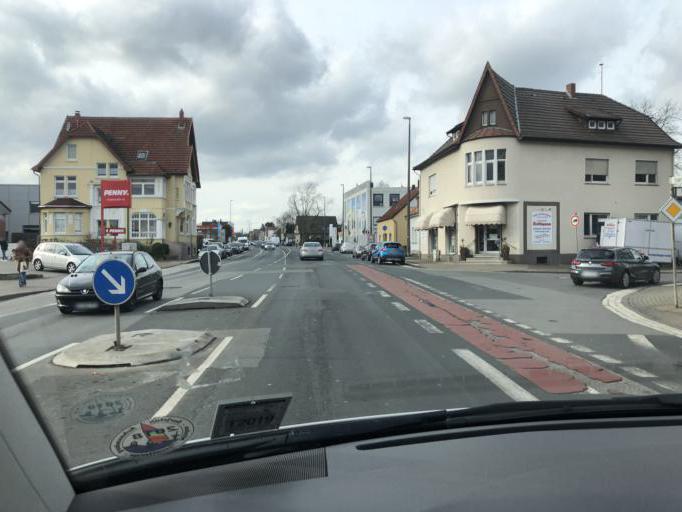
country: DE
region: North Rhine-Westphalia
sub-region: Regierungsbezirk Detmold
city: Herford
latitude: 52.1202
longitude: 8.6532
